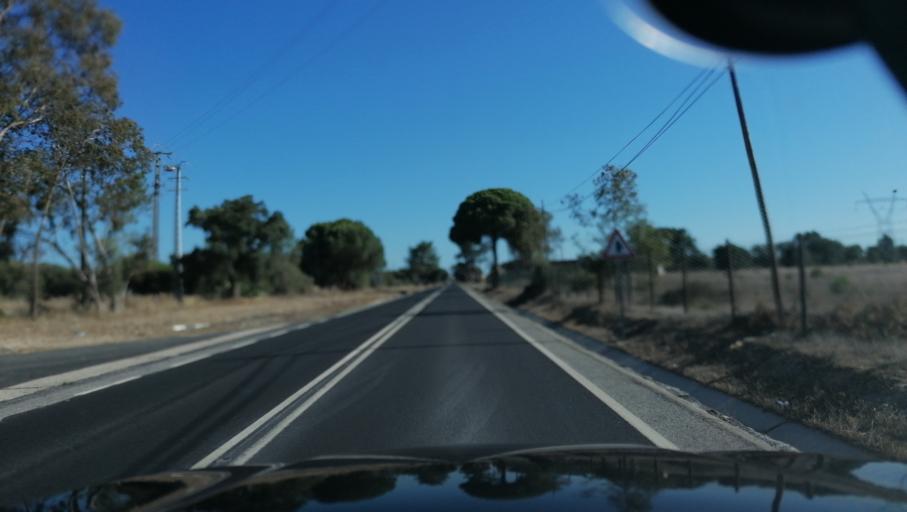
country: PT
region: Santarem
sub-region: Benavente
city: Poceirao
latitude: 38.8300
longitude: -8.8809
